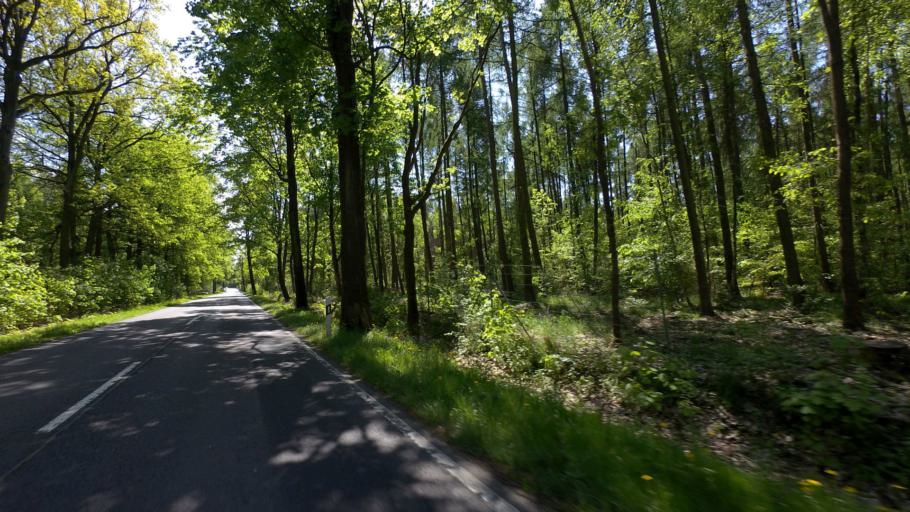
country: DE
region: Brandenburg
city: Schulzendorf
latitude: 52.3233
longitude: 13.5860
